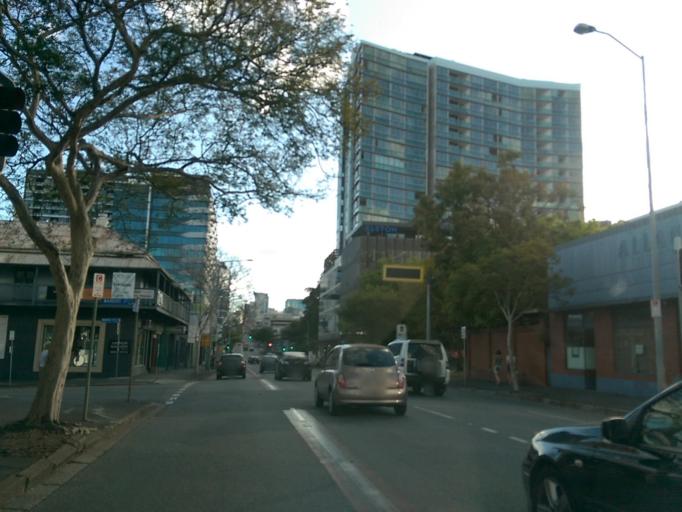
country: AU
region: Queensland
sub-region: Brisbane
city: Fortitude Valley
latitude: -27.4543
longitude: 153.0391
